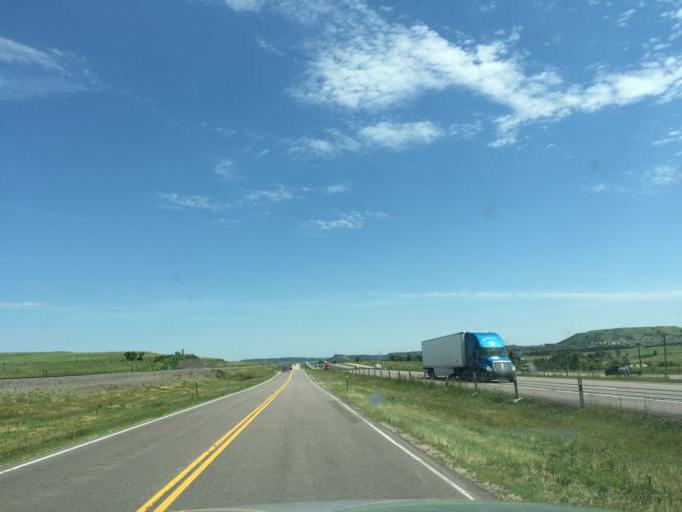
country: US
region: Colorado
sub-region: Douglas County
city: Castle Rock
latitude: 39.3174
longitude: -104.8841
